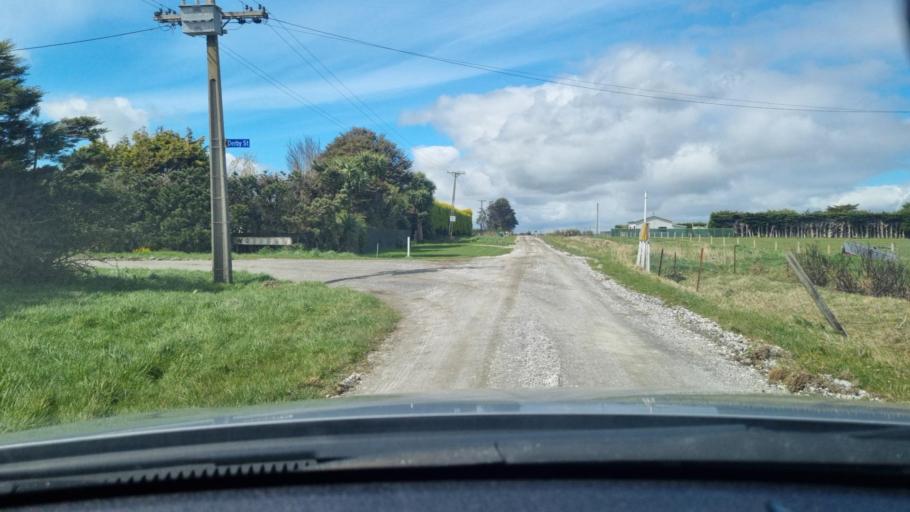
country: NZ
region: Southland
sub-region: Invercargill City
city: Invercargill
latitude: -46.4774
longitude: 168.3910
